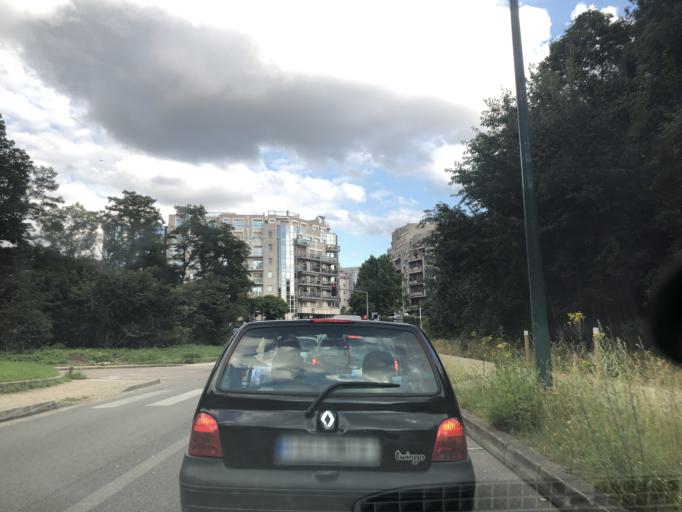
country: FR
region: Ile-de-France
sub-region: Departement du Val-de-Marne
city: Joinville-le-Pont
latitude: 48.8196
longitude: 2.4619
